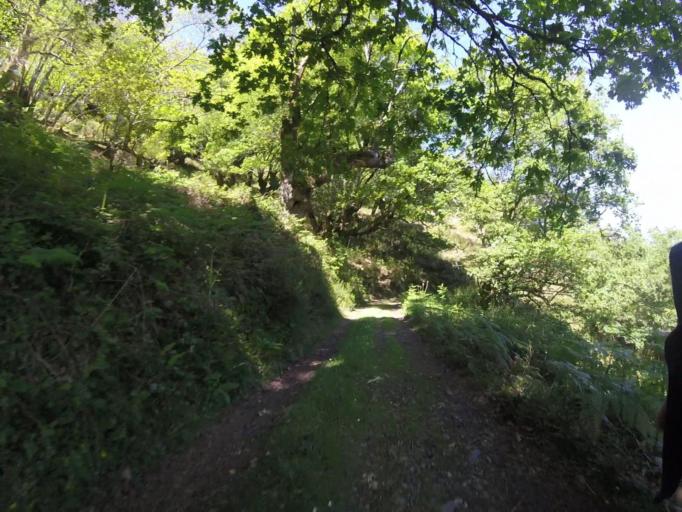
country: ES
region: Navarre
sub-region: Provincia de Navarra
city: Lesaka
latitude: 43.2457
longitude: -1.7502
